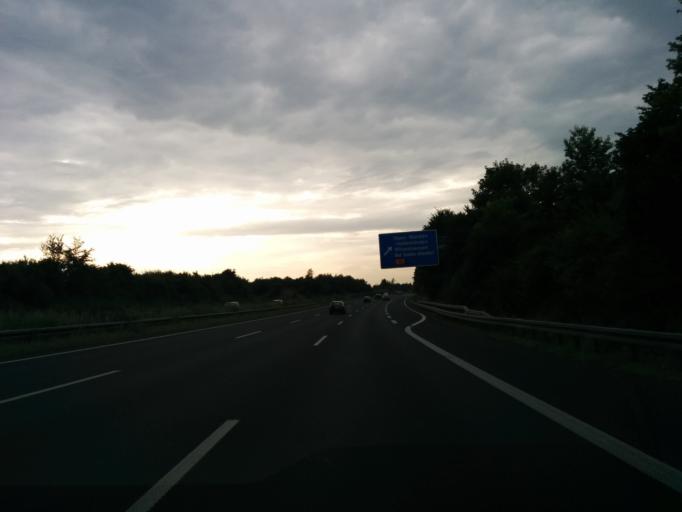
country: DE
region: Lower Saxony
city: Scheden
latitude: 51.3959
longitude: 9.7712
